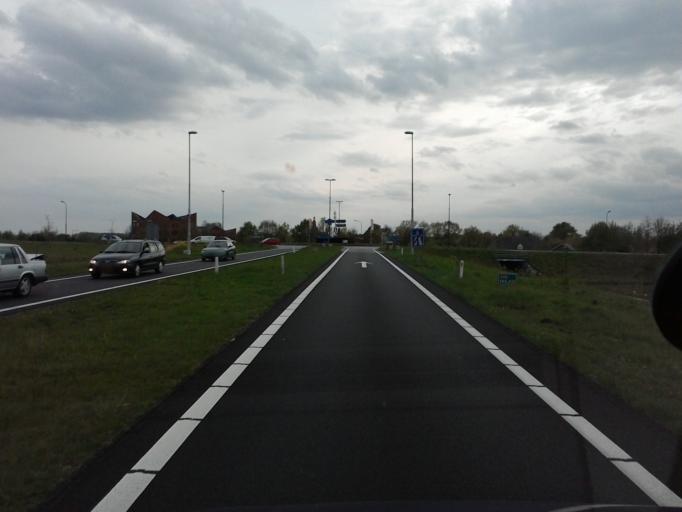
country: NL
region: North Brabant
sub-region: Gemeente Sint-Oedenrode
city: Sint-Oedenrode
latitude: 51.5725
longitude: 5.4783
